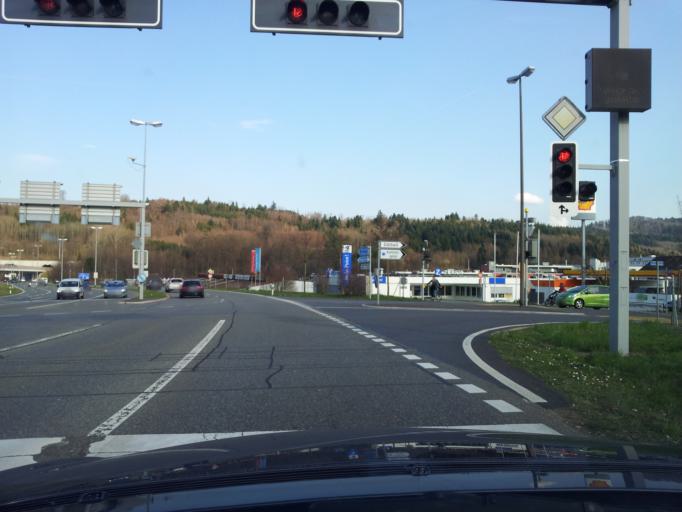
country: CH
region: Aargau
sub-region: Bezirk Baden
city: Baden
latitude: 47.4569
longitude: 8.2817
